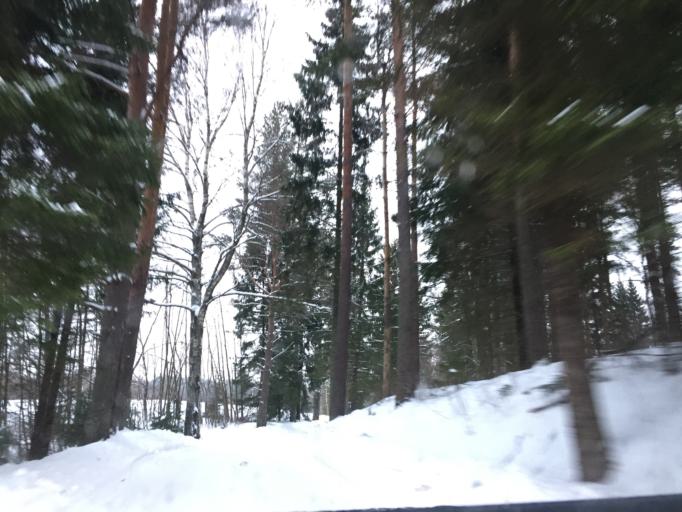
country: LV
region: Amatas Novads
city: Drabesi
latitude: 57.2042
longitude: 25.2979
